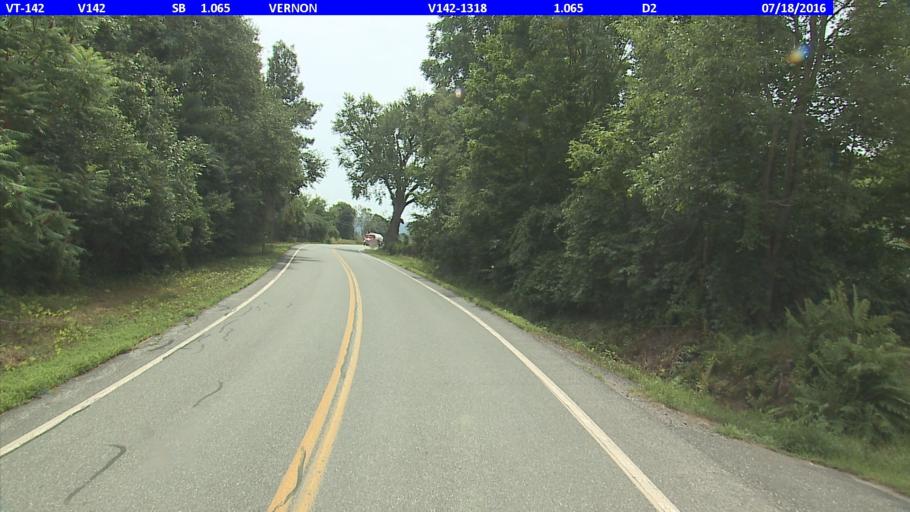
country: US
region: New Hampshire
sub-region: Cheshire County
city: Hinsdale
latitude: 42.7410
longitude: -72.4727
